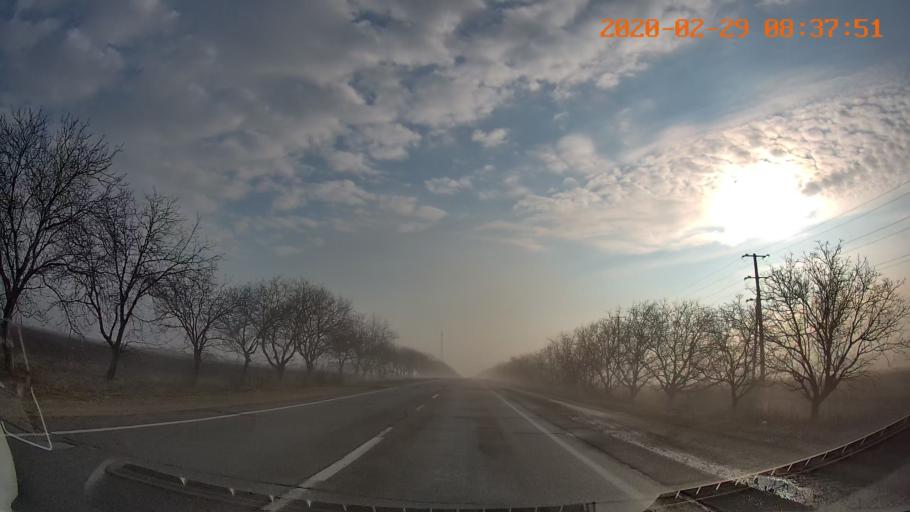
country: MD
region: Anenii Noi
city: Varnita
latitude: 46.9214
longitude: 29.3673
